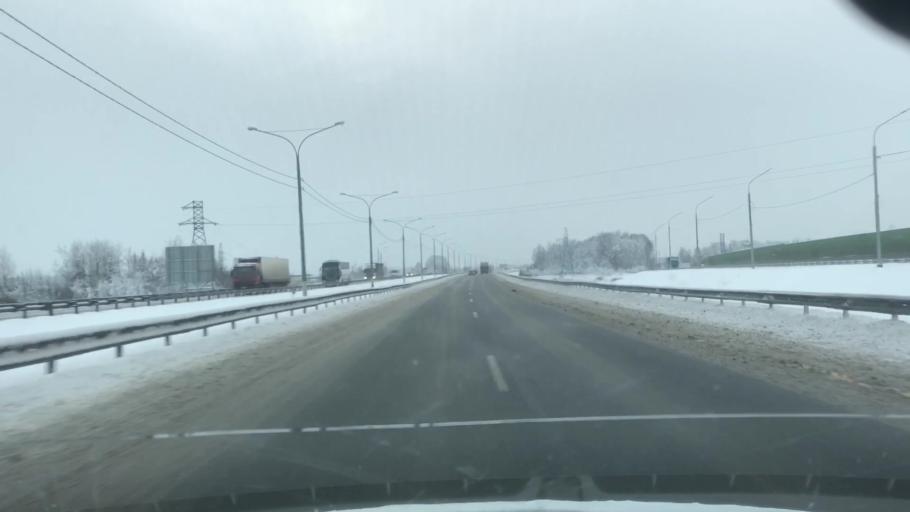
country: RU
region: Moskovskaya
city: Mikhnevo
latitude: 55.1567
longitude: 37.9273
